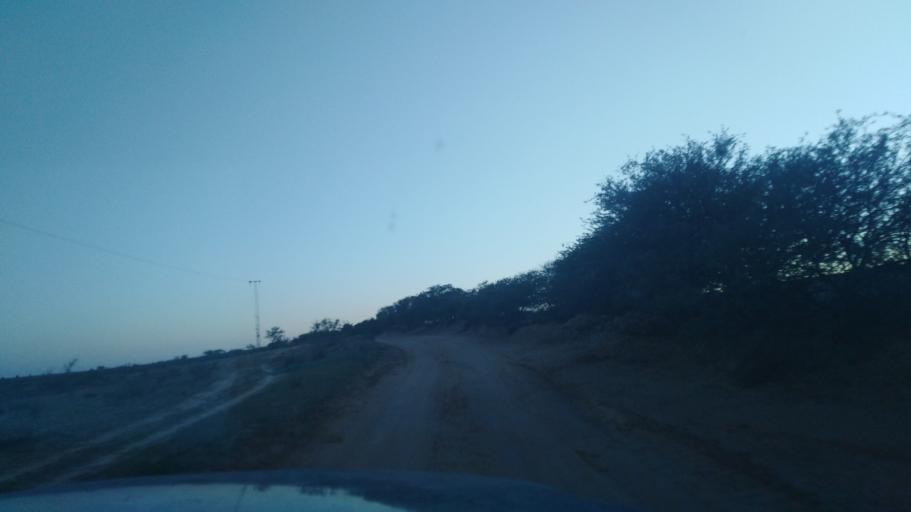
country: TN
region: Safaqis
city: Sfax
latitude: 34.7344
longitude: 10.4449
